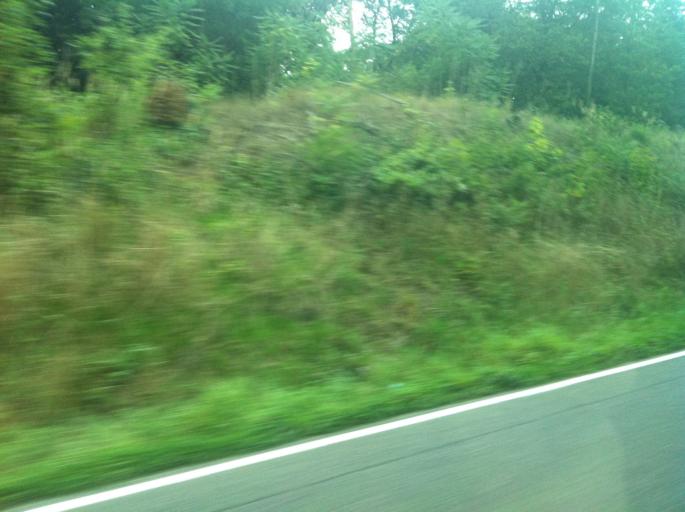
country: DE
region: Rheinland-Pfalz
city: Budenheim
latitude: 50.0107
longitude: 8.1770
